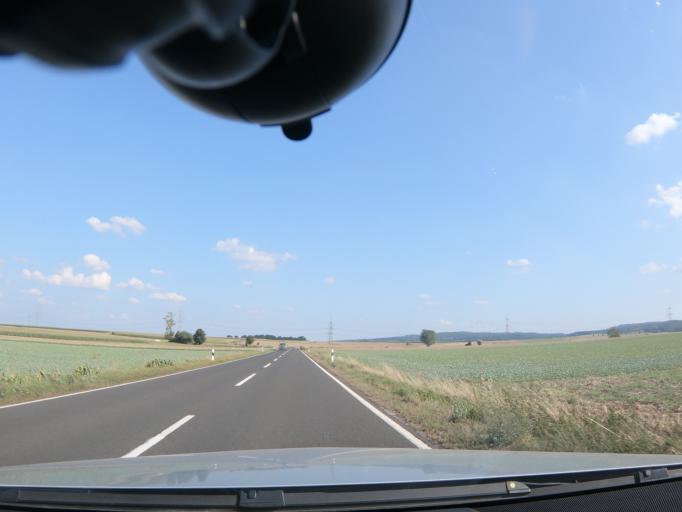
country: DE
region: Hesse
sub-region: Regierungsbezirk Giessen
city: Ebsdorfergrund
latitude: 50.7806
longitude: 8.8506
